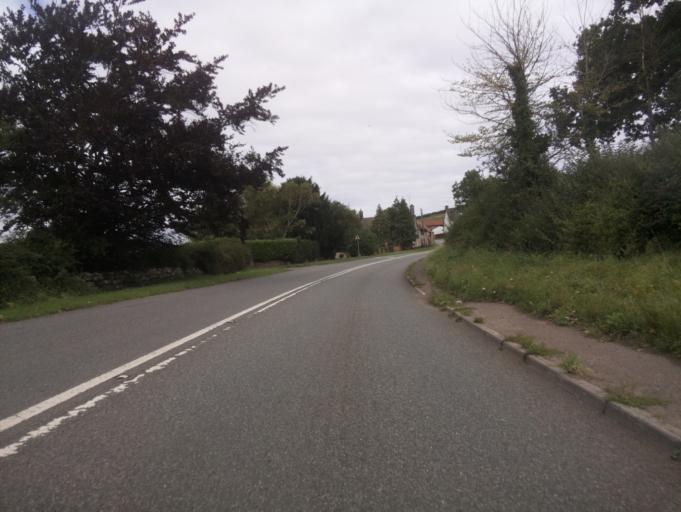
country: GB
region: England
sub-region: Devon
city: Bradninch
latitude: 50.8298
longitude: -3.3937
